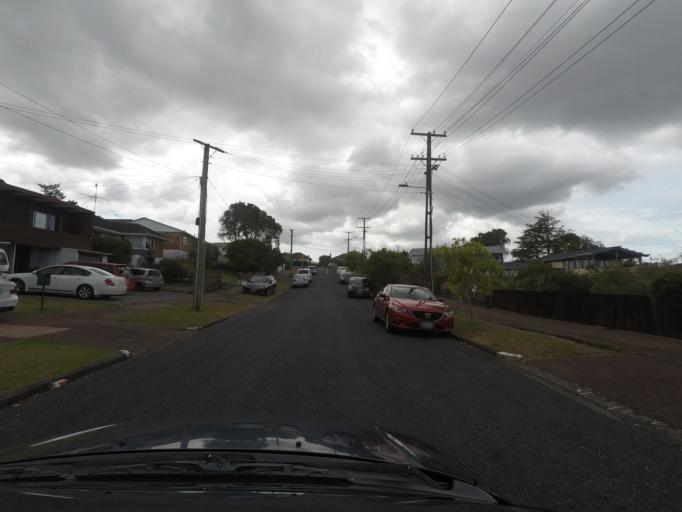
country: NZ
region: Auckland
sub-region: Auckland
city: Rosebank
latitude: -36.9089
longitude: 174.7137
